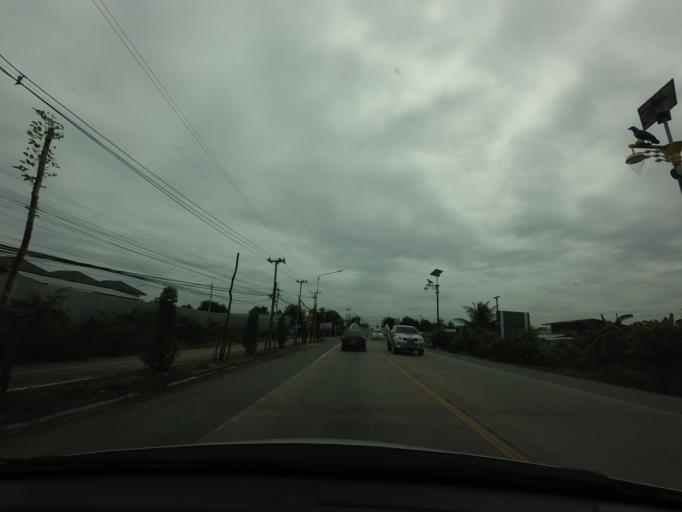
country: TH
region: Pathum Thani
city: Lam Luk Ka
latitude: 13.9292
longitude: 100.7267
